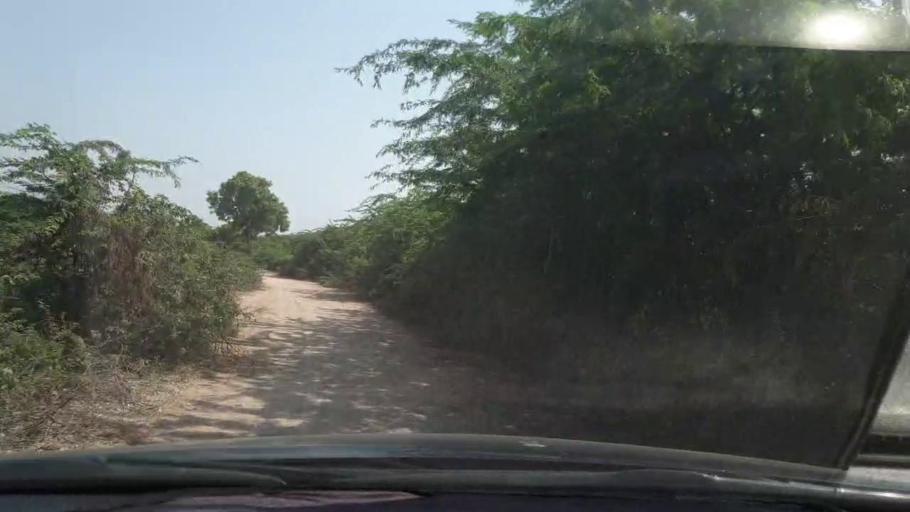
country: PK
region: Sindh
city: Naukot
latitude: 24.8093
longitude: 69.2649
